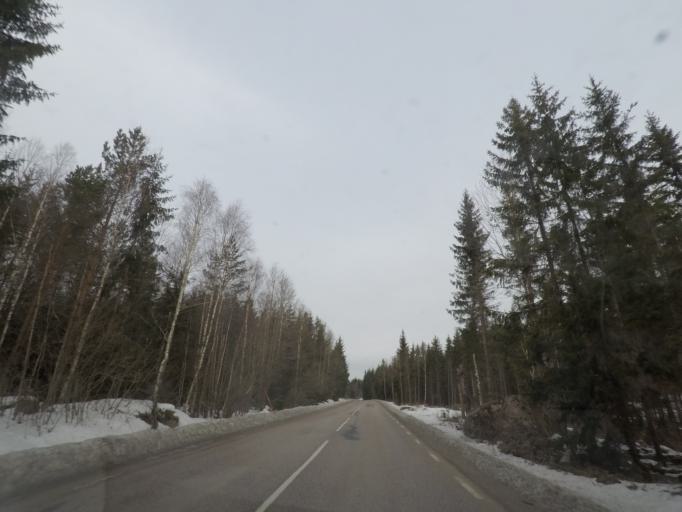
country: SE
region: Vaestmanland
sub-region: Vasteras
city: Skultuna
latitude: 59.7453
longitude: 16.3626
